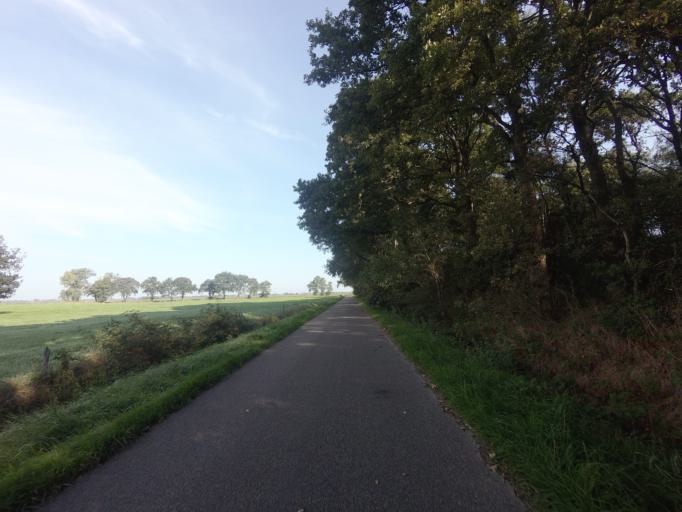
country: NL
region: Groningen
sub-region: Gemeente Leek
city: Leek
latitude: 53.1652
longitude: 6.4323
